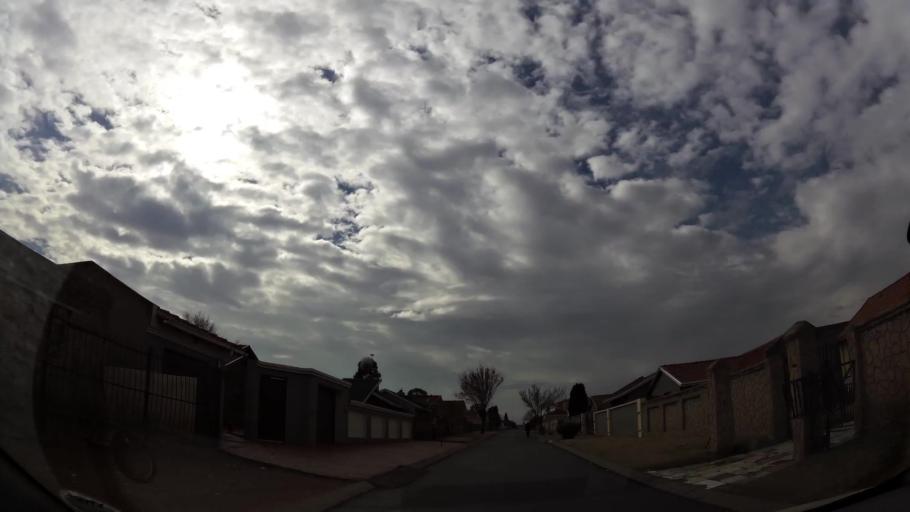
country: ZA
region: Gauteng
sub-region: Ekurhuleni Metropolitan Municipality
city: Germiston
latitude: -26.3295
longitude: 28.1759
